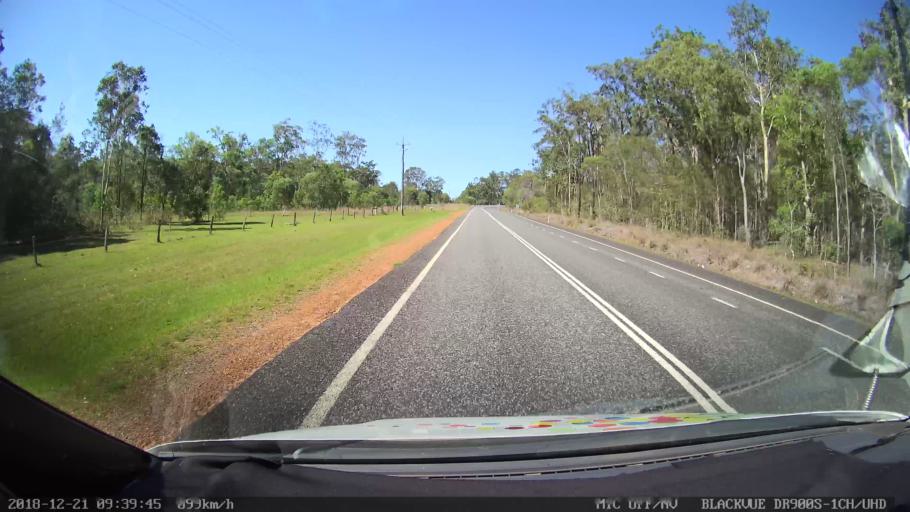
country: AU
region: New South Wales
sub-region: Clarence Valley
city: Grafton
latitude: -29.5647
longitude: 152.9692
